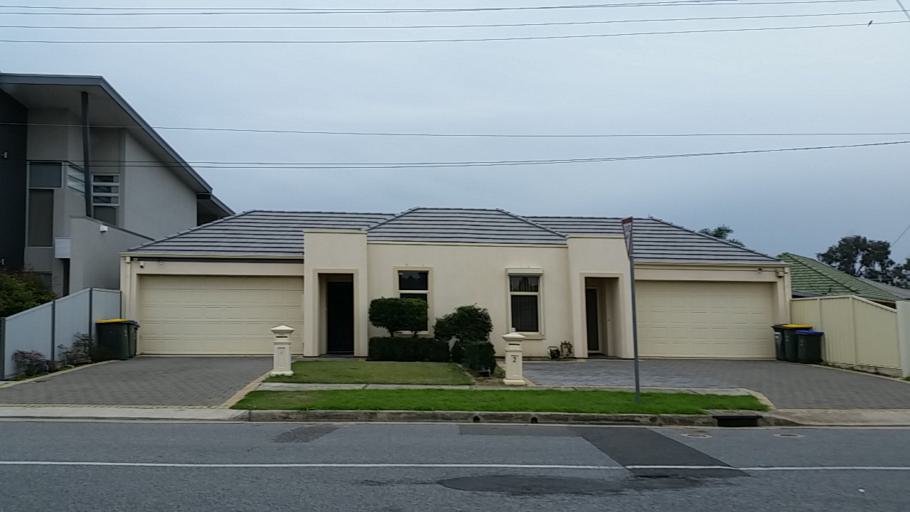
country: AU
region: South Australia
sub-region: Charles Sturt
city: Royal Park
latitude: -34.8733
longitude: 138.5047
